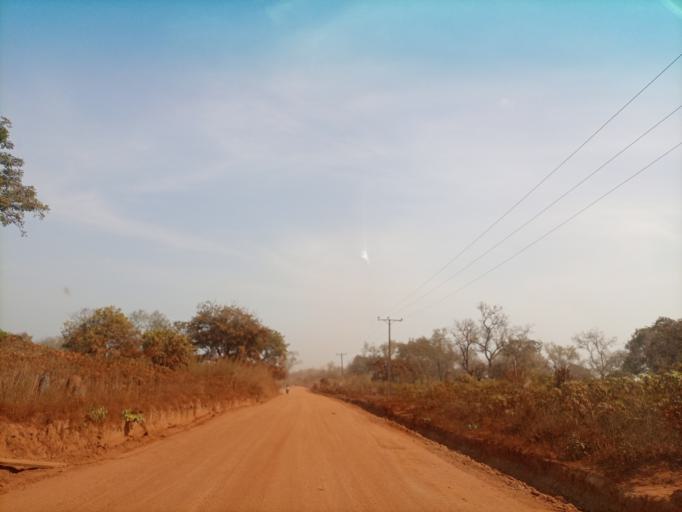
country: NG
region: Enugu
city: Eha Amufu
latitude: 6.6723
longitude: 7.7356
